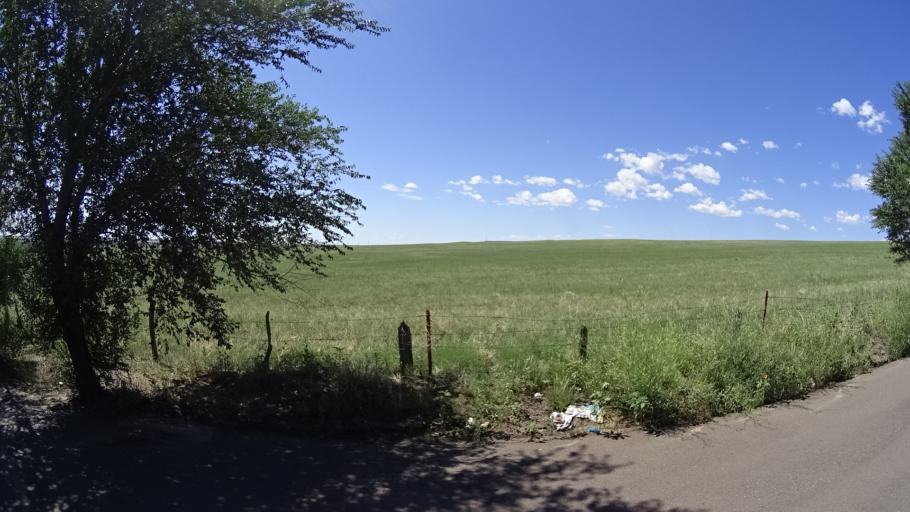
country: US
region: Colorado
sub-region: El Paso County
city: Security-Widefield
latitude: 38.7810
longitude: -104.6784
